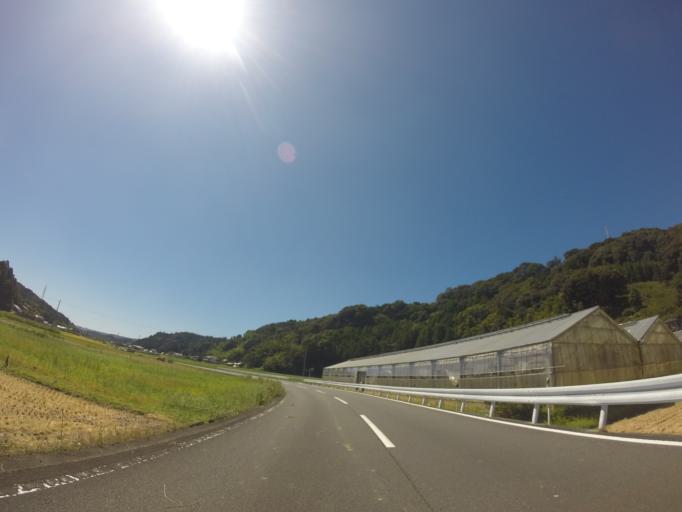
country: JP
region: Shizuoka
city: Kanaya
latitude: 34.8713
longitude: 138.1340
